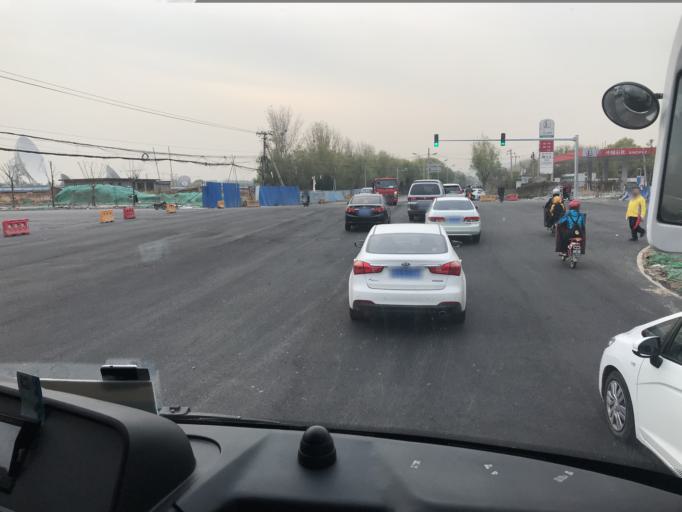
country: CN
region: Beijing
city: Wenquan
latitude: 40.0917
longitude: 116.2095
